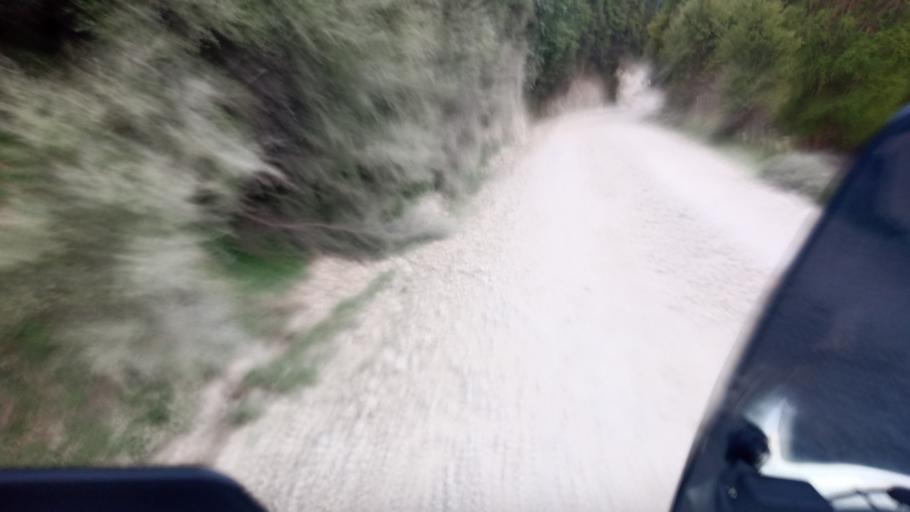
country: NZ
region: Gisborne
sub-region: Gisborne District
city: Gisborne
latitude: -38.4747
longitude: 177.9753
